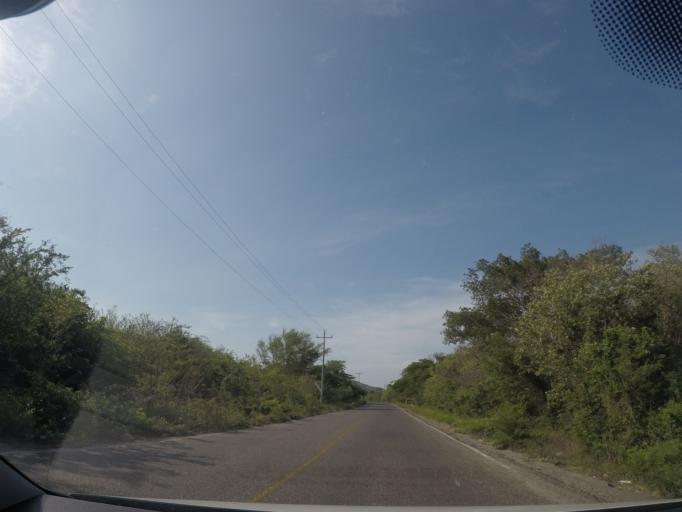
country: MX
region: Oaxaca
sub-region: Salina Cruz
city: Salina Cruz
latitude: 16.2266
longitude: -95.1368
